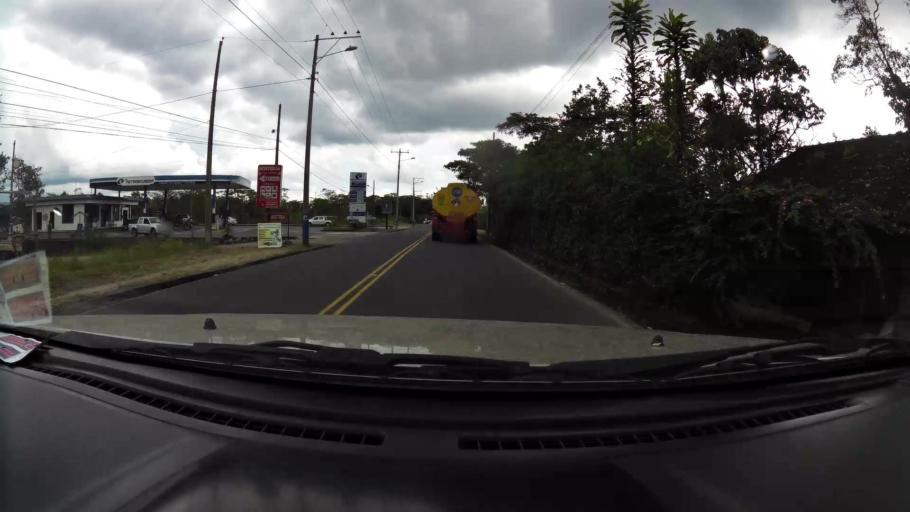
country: EC
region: Pastaza
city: Puyo
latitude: -1.4562
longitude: -78.1206
